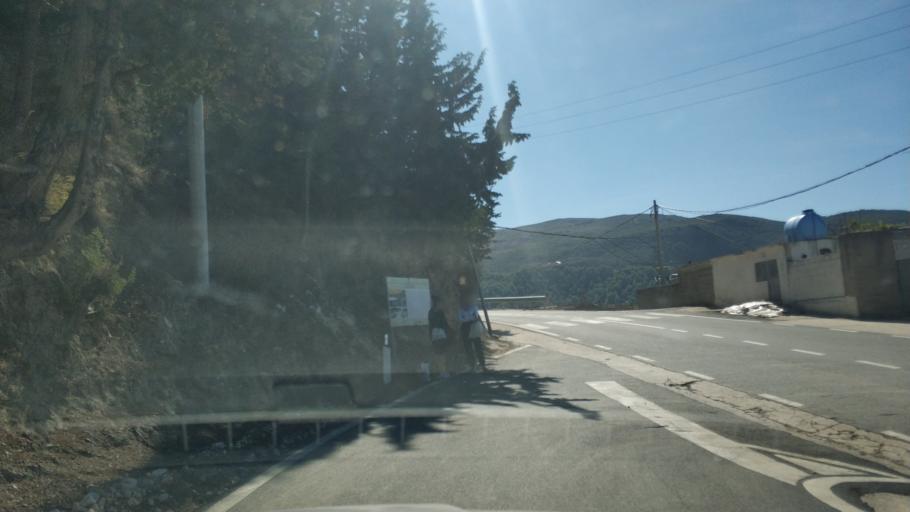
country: AL
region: Vlore
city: Vlore
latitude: 40.4444
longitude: 19.5186
